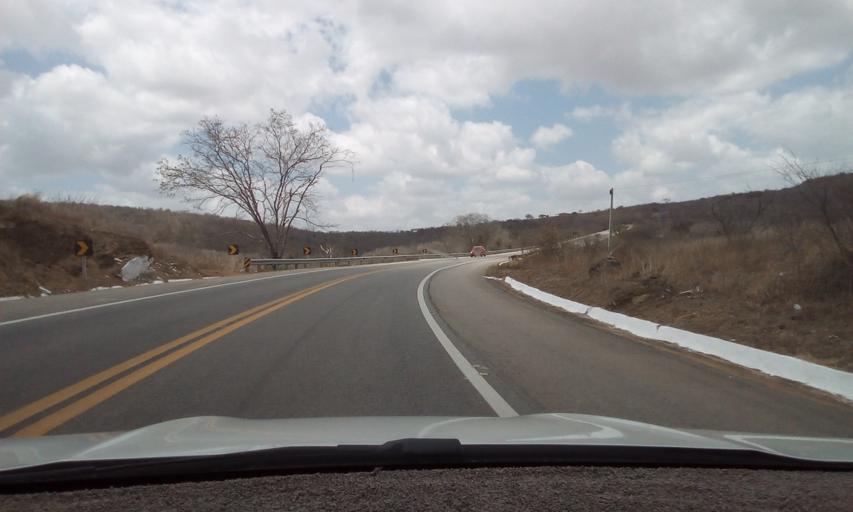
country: BR
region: Paraiba
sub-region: Boqueirao
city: Boqueirao
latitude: -7.6817
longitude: -36.0598
